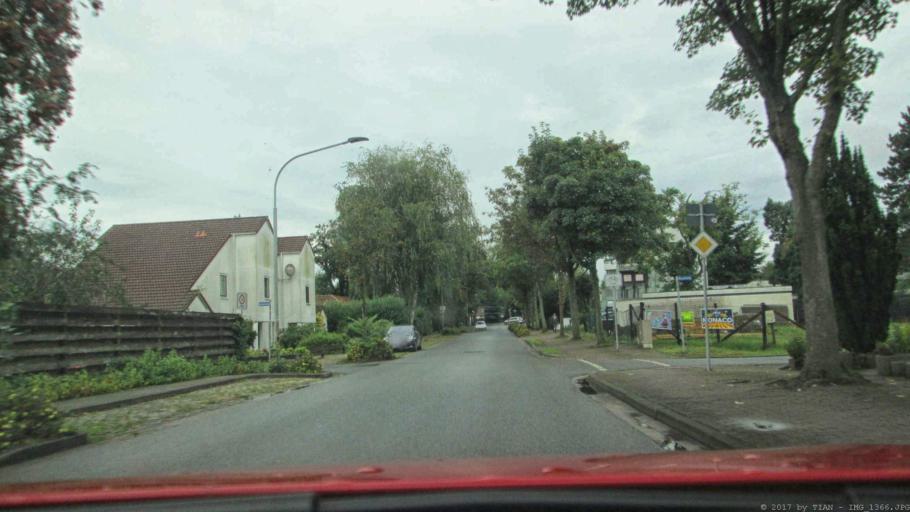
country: DE
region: Lower Saxony
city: Wittingen
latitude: 52.7282
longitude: 10.7444
